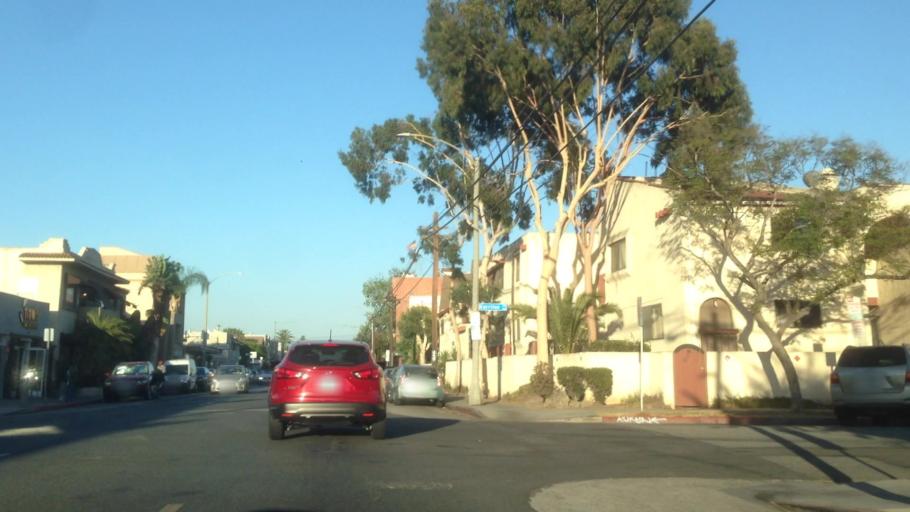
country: US
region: California
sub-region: Los Angeles County
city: Long Beach
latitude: 33.7717
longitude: -118.1783
